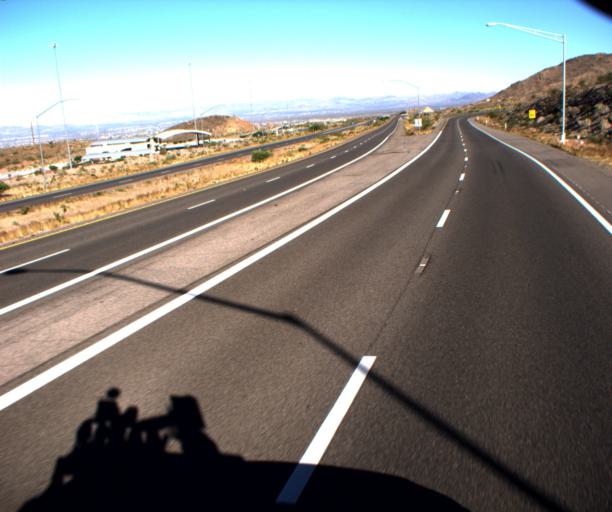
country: US
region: Arizona
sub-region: Mohave County
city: Kingman
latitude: 35.2174
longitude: -114.1174
